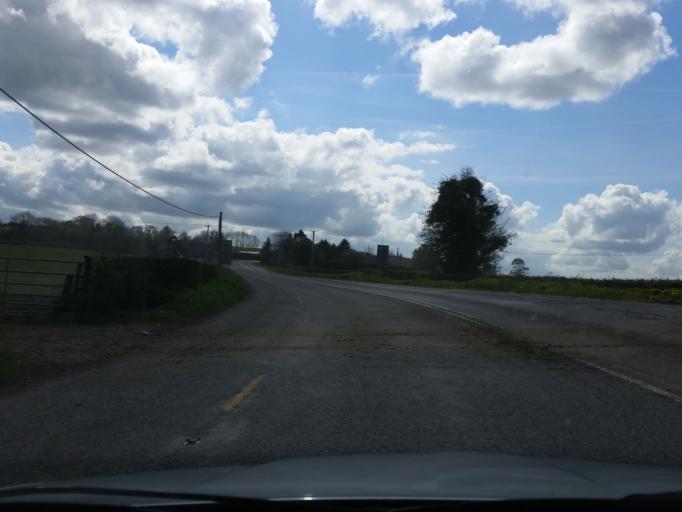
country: IE
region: Leinster
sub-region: An Mhi
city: Slane
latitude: 53.6963
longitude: -6.5390
